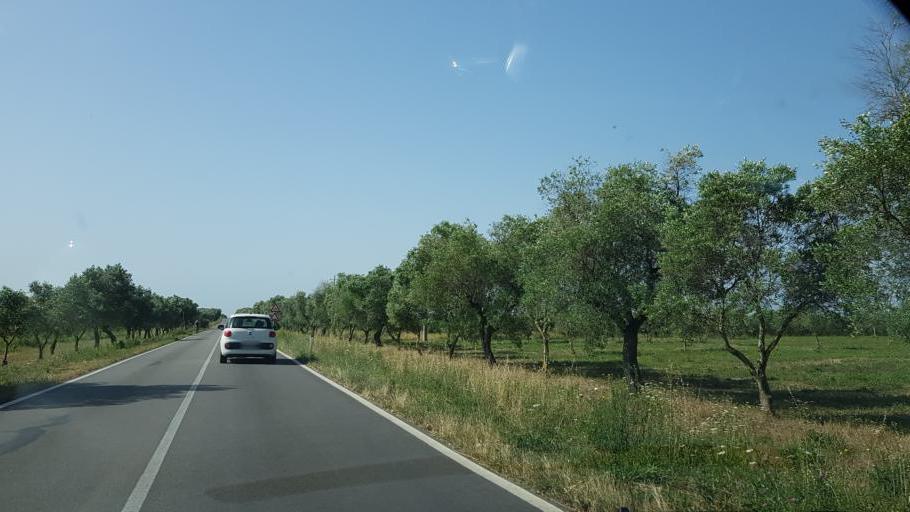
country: IT
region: Apulia
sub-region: Provincia di Brindisi
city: San Pancrazio Salentino
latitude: 40.3739
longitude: 17.8385
